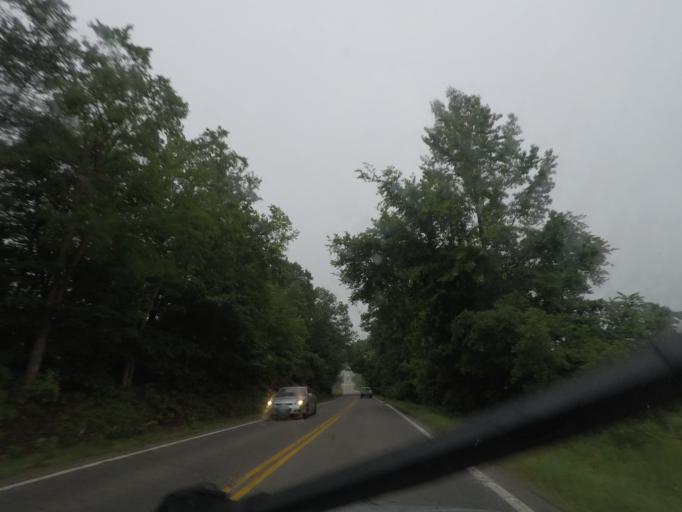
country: US
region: Virginia
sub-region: Prince Edward County
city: Farmville
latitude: 37.3376
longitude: -78.4697
